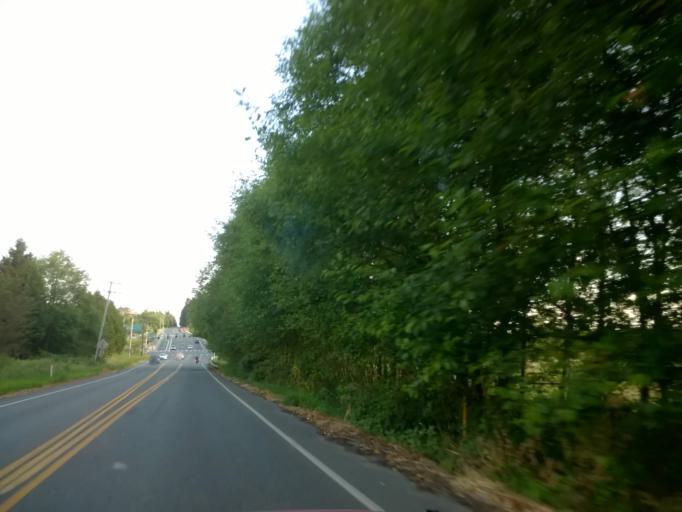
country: US
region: Washington
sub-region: King County
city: Redmond
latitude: 47.7122
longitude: -122.1318
